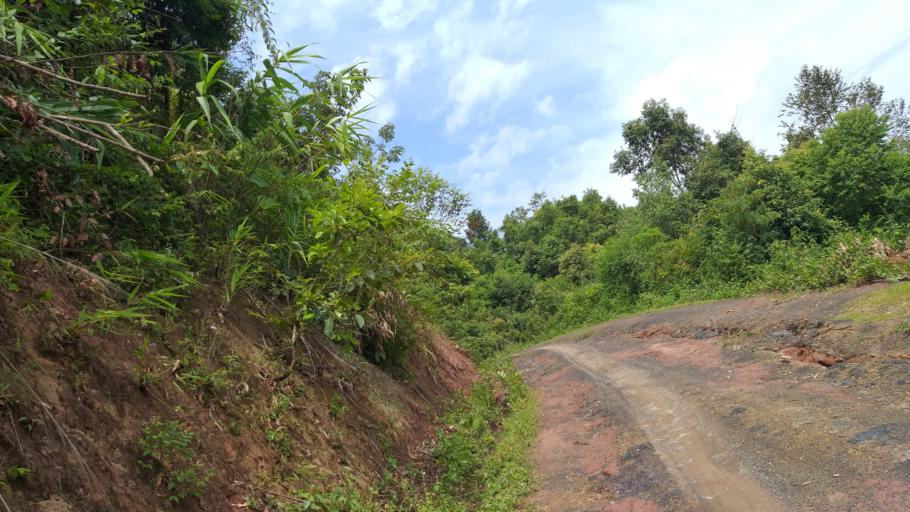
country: VN
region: Huyen Dien Bien
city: Dien Bien Phu
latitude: 21.4064
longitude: 102.6808
